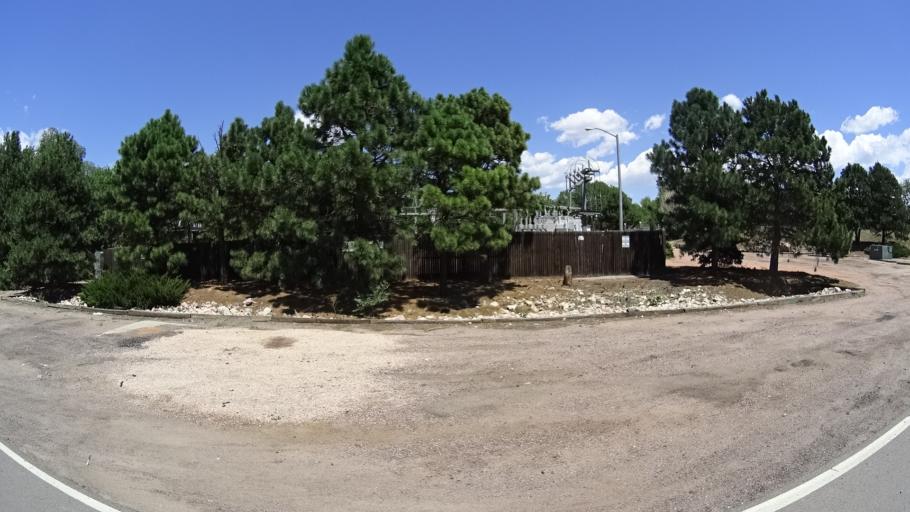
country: US
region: Colorado
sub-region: El Paso County
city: Stratmoor
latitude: 38.7978
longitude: -104.7826
